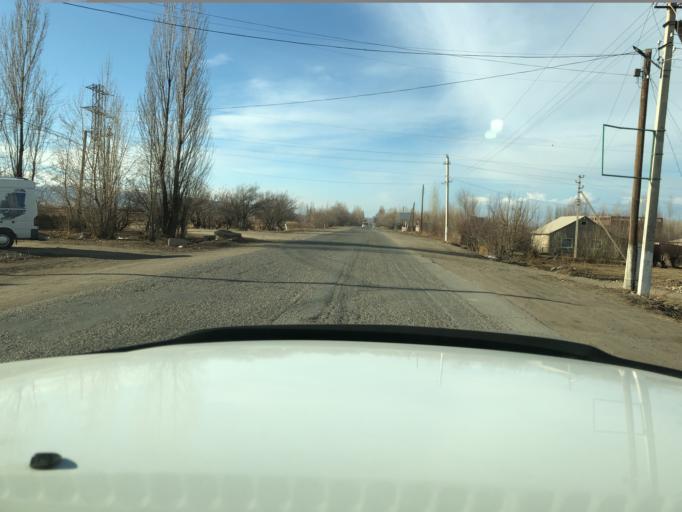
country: KG
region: Ysyk-Koel
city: Pokrovka
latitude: 42.3331
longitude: 77.9838
